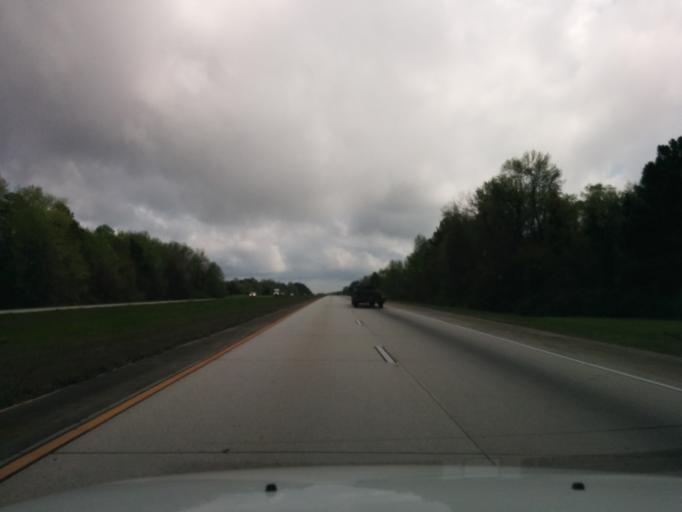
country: US
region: Georgia
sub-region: Evans County
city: Claxton
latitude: 32.3199
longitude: -81.9149
